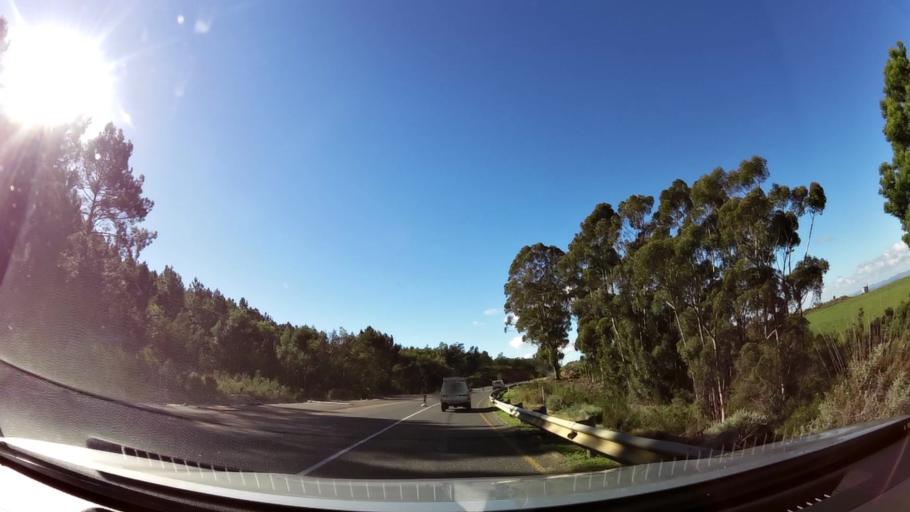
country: ZA
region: Western Cape
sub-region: Overberg District Municipality
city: Caledon
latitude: -34.2065
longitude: 19.5756
